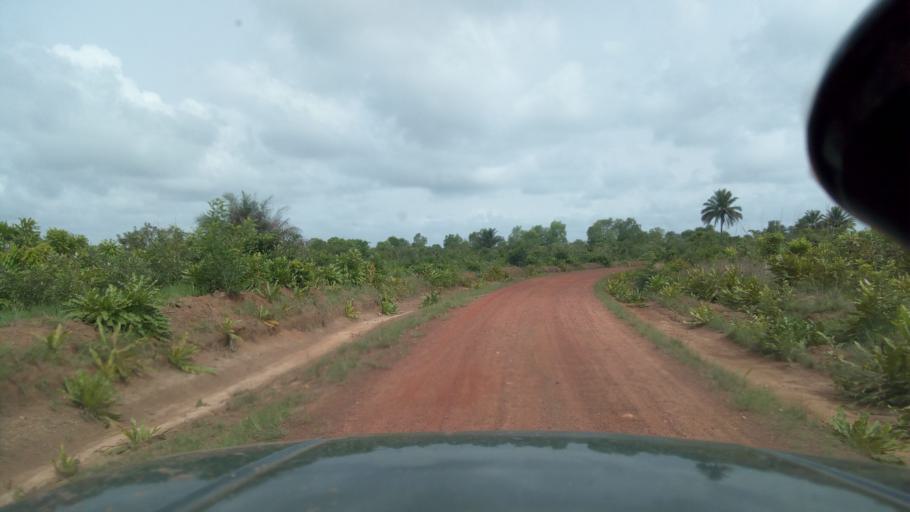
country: SL
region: Northern Province
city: Port Loko
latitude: 8.7693
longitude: -12.9122
